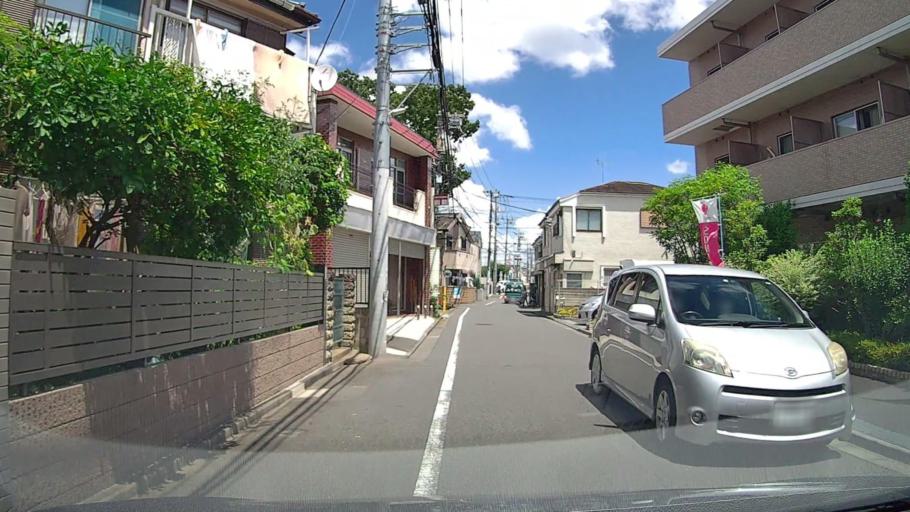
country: JP
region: Tokyo
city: Tanashicho
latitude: 35.7423
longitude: 139.5506
